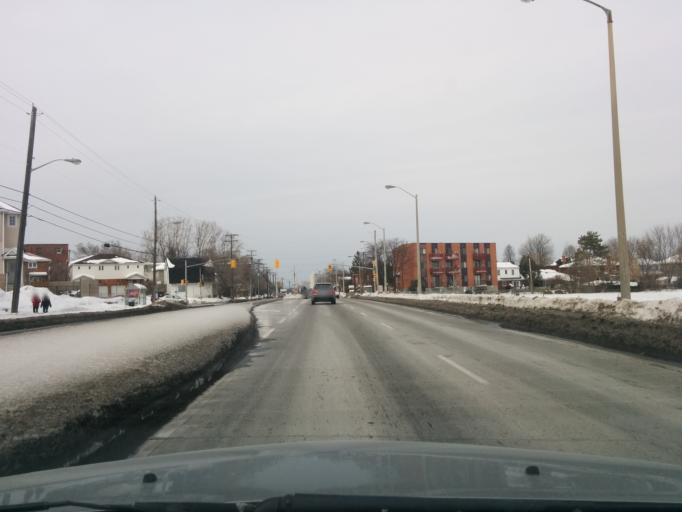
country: CA
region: Ontario
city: Ottawa
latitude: 45.3725
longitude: -75.7324
